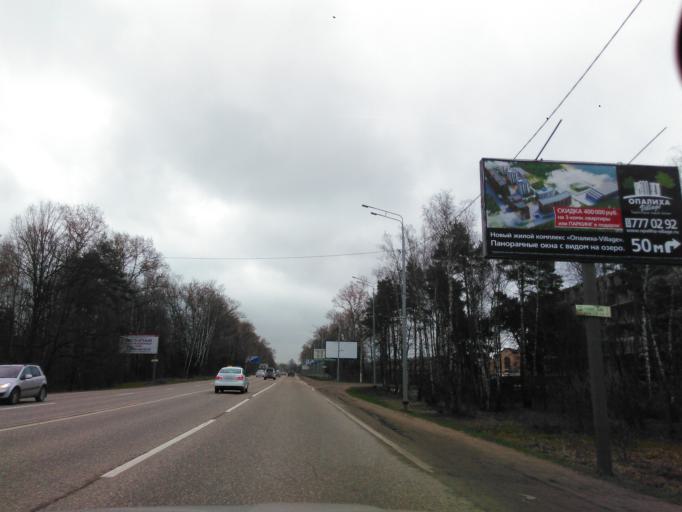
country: RU
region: Moskovskaya
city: Opalikha
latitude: 55.8403
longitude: 37.2271
